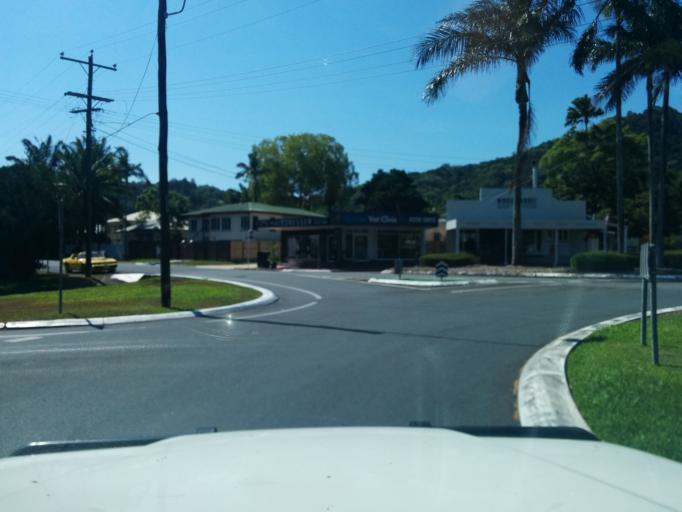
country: AU
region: Queensland
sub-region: Cairns
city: Redlynch
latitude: -16.9005
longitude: 145.7315
